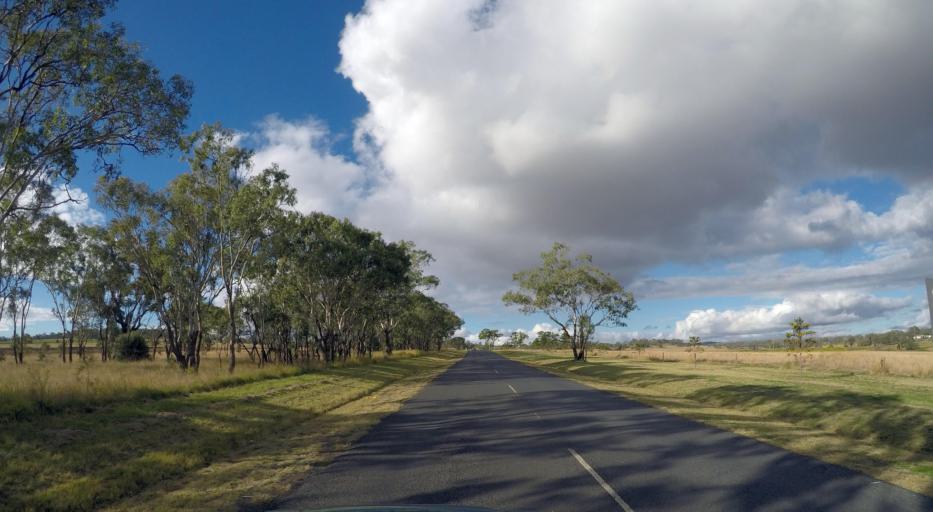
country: AU
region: Queensland
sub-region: Toowoomba
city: Westbrook
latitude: -27.7060
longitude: 151.6517
